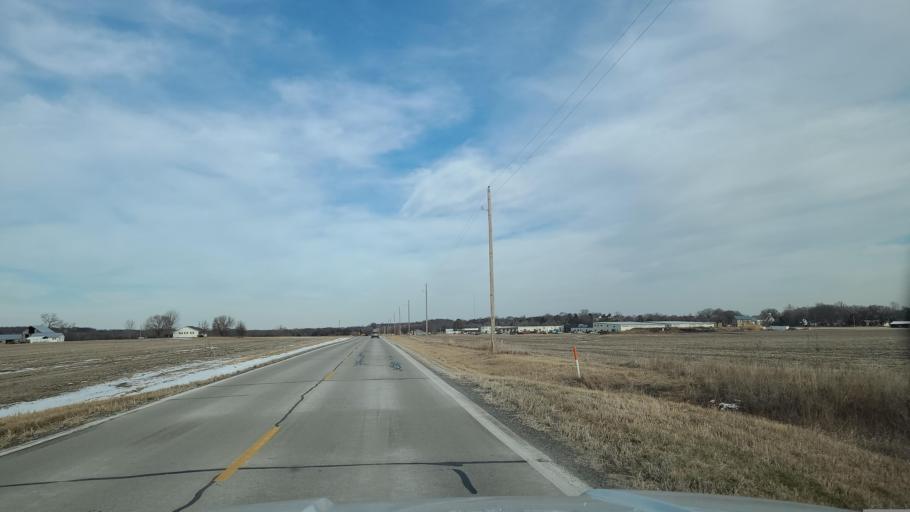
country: US
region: Kansas
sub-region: Douglas County
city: Baldwin City
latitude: 38.8337
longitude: -95.1864
